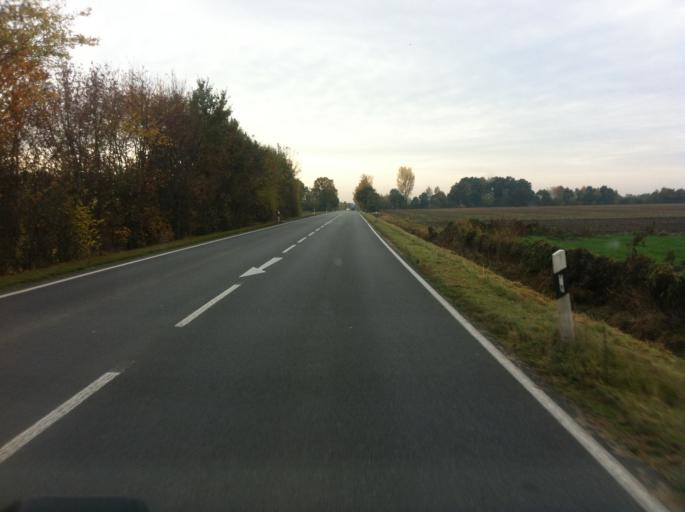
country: NL
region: Overijssel
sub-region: Gemeente Enschede
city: Enschede
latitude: 52.1205
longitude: 6.9053
